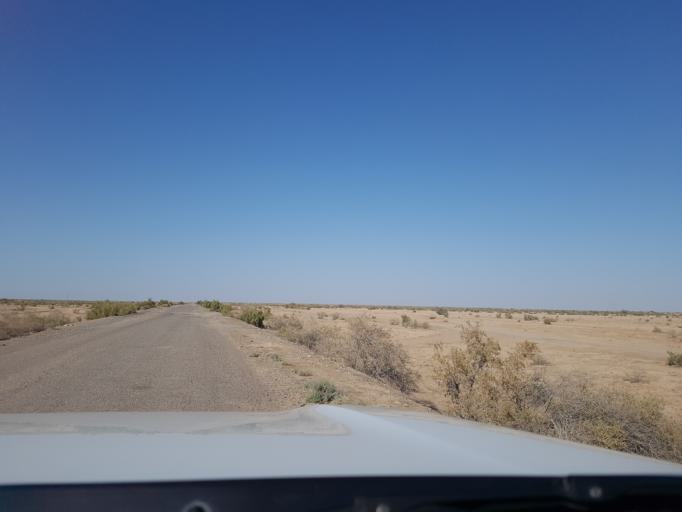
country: IR
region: Razavi Khorasan
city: Sarakhs
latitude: 36.8349
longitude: 61.3309
